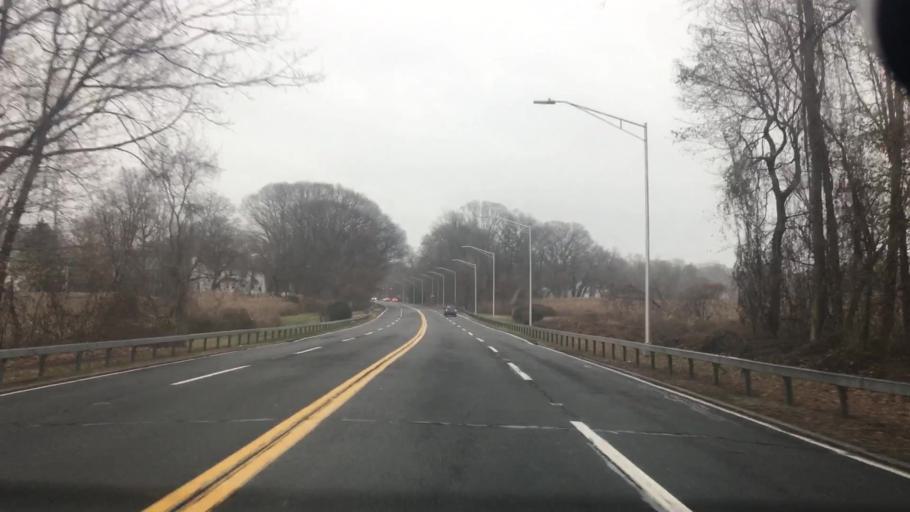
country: US
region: New York
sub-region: Westchester County
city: Rye
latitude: 40.9697
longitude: -73.6912
